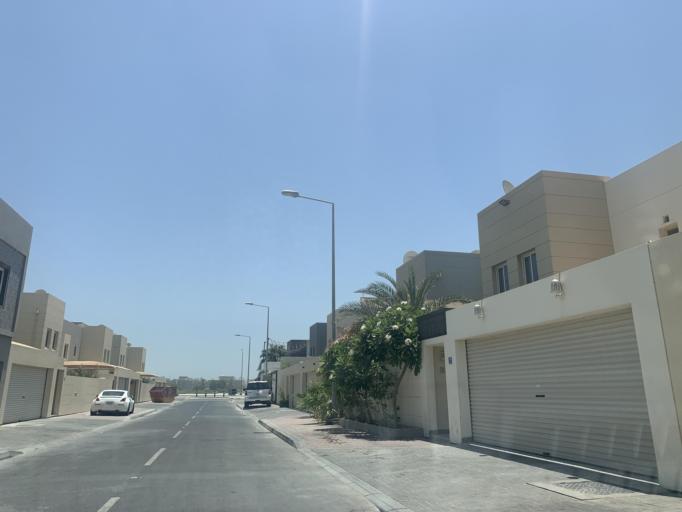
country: BH
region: Manama
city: Jidd Hafs
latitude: 26.2366
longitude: 50.4642
